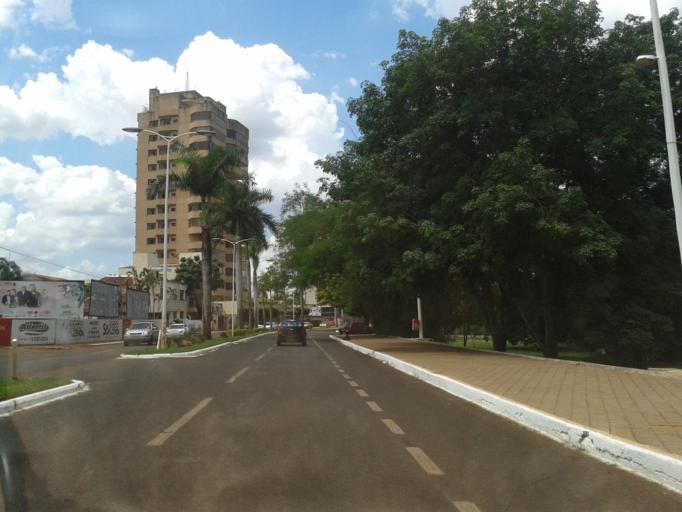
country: BR
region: Goias
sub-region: Itumbiara
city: Itumbiara
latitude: -18.4143
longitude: -49.2116
